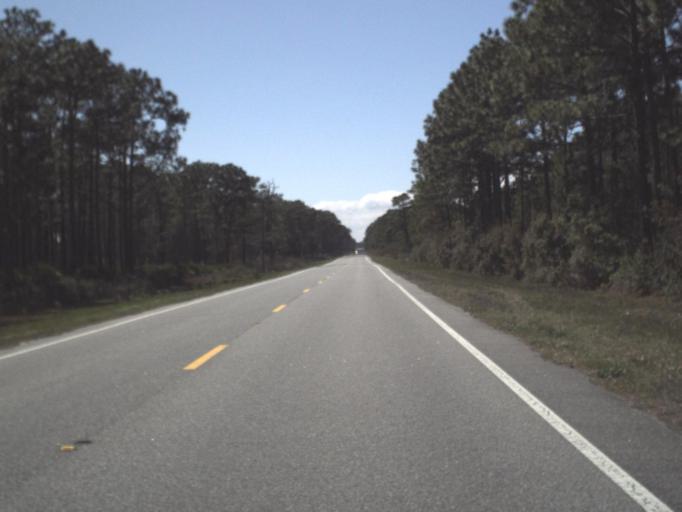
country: US
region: Florida
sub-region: Franklin County
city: Carrabelle
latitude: 29.9227
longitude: -84.4887
